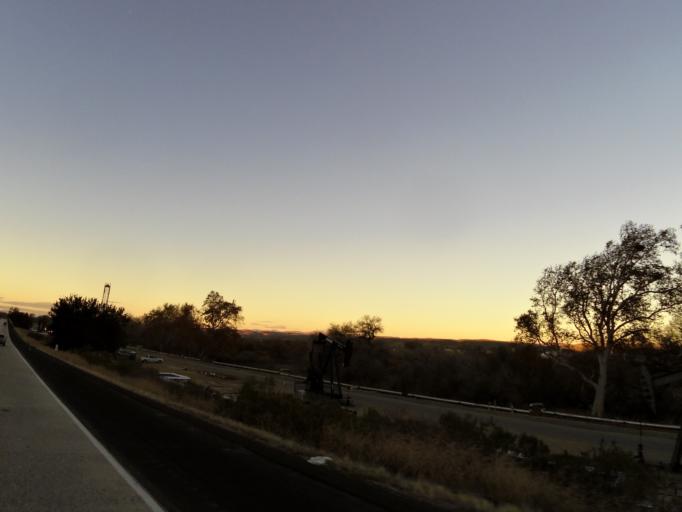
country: US
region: California
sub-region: San Luis Obispo County
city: Lake Nacimiento
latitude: 35.9536
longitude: -120.8800
